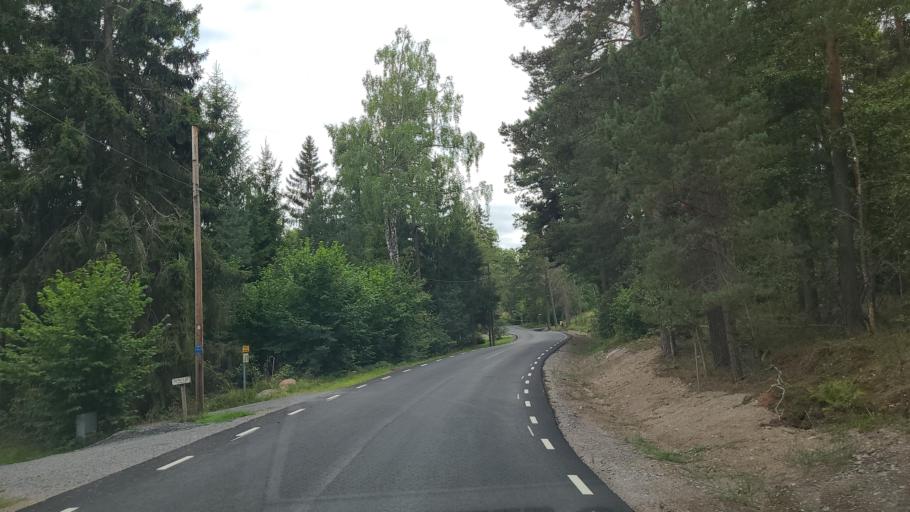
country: SE
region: Stockholm
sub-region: Upplands-Bro Kommun
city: Bro
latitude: 59.4811
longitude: 17.5984
